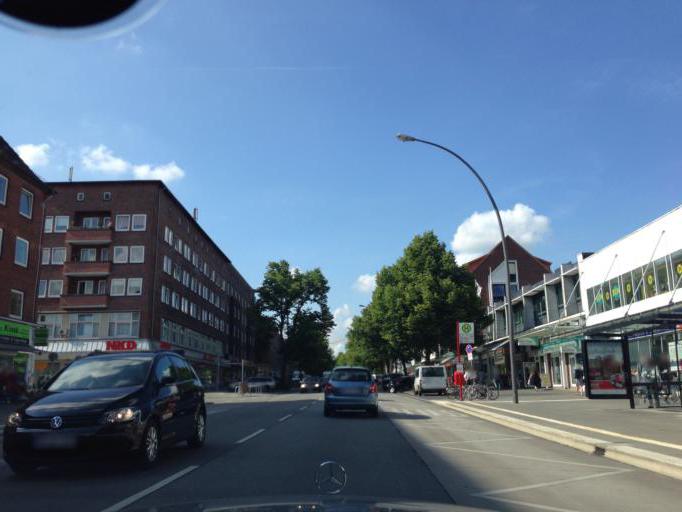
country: DE
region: Hamburg
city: Barmbek-Nord
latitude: 53.5941
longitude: 10.0441
